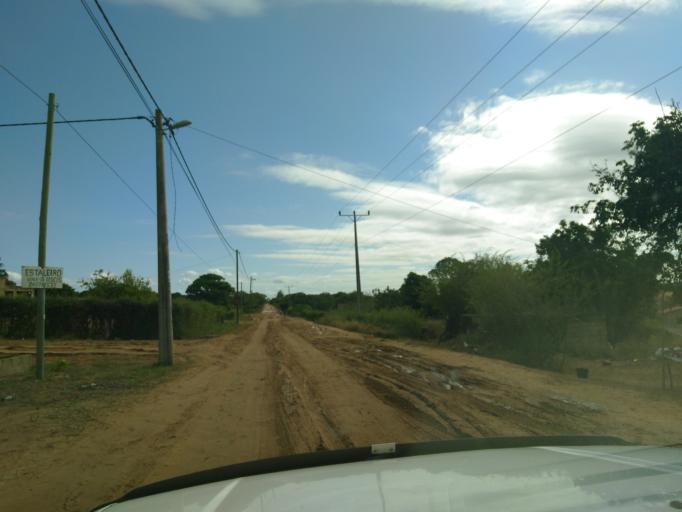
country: MZ
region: Maputo City
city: Maputo
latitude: -26.0016
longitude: 32.5435
